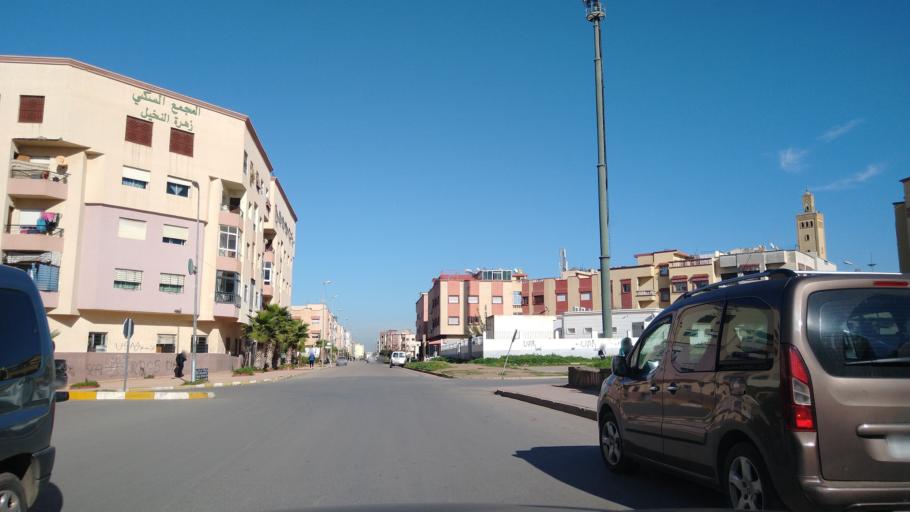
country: MA
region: Rabat-Sale-Zemmour-Zaer
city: Sale
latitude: 34.0758
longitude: -6.7886
